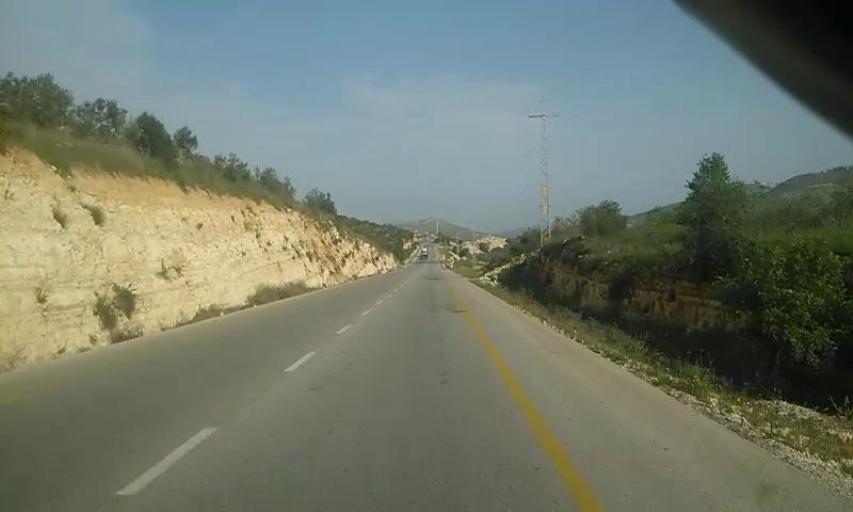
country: PS
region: West Bank
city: `Asirah al Qibliyah
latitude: 32.1888
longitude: 35.2135
